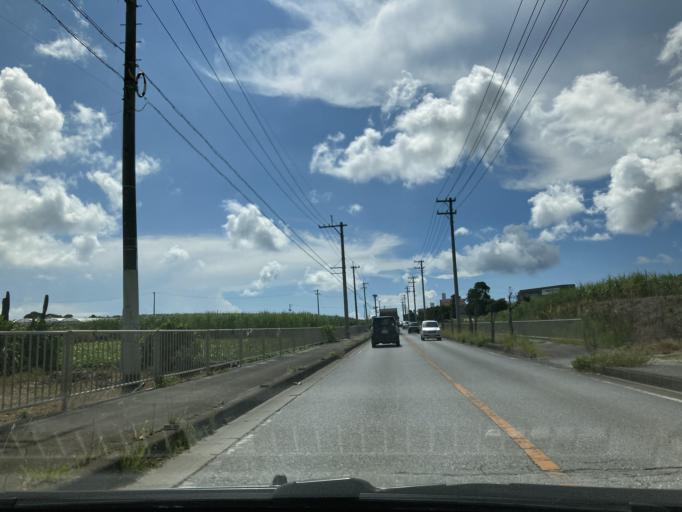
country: JP
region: Okinawa
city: Itoman
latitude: 26.1420
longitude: 127.7277
